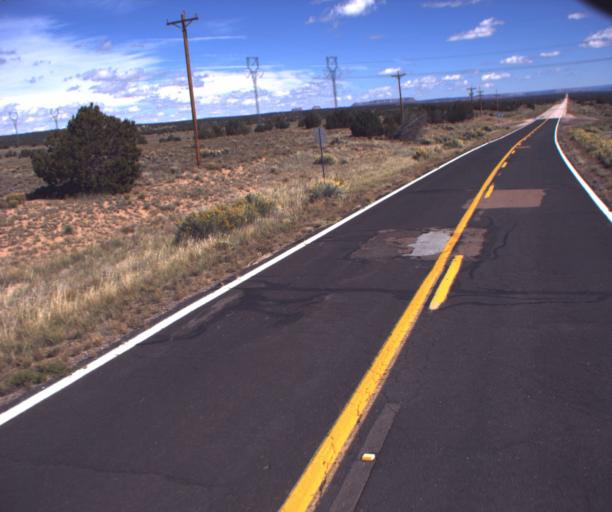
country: US
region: New Mexico
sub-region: McKinley County
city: Zuni Pueblo
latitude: 35.0193
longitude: -109.0480
